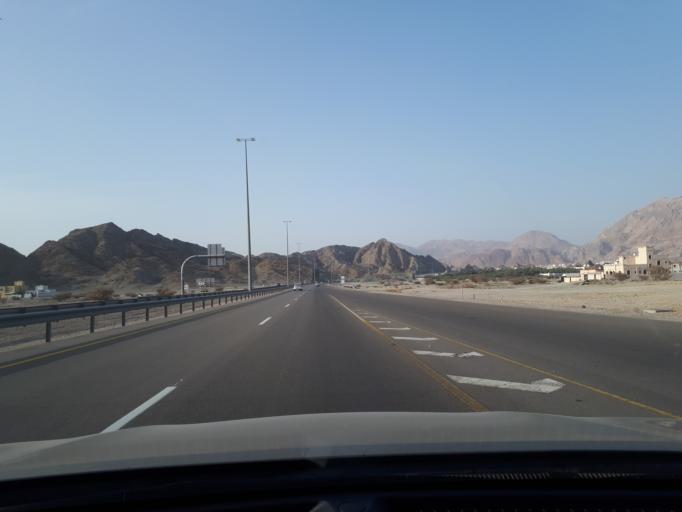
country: OM
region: Muhafazat Masqat
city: Bawshar
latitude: 23.4173
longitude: 58.4975
